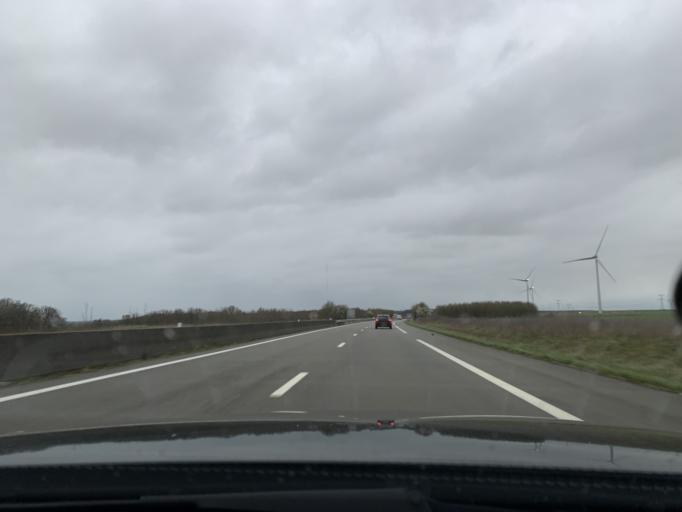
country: FR
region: Picardie
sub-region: Departement de l'Oise
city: Breteuil
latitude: 49.6314
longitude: 2.2092
